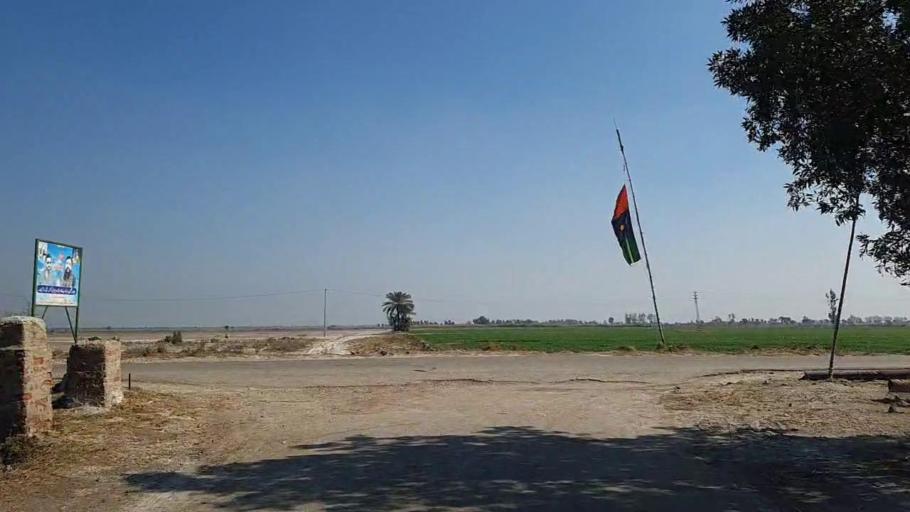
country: PK
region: Sindh
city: Nawabshah
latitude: 26.3414
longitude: 68.4378
